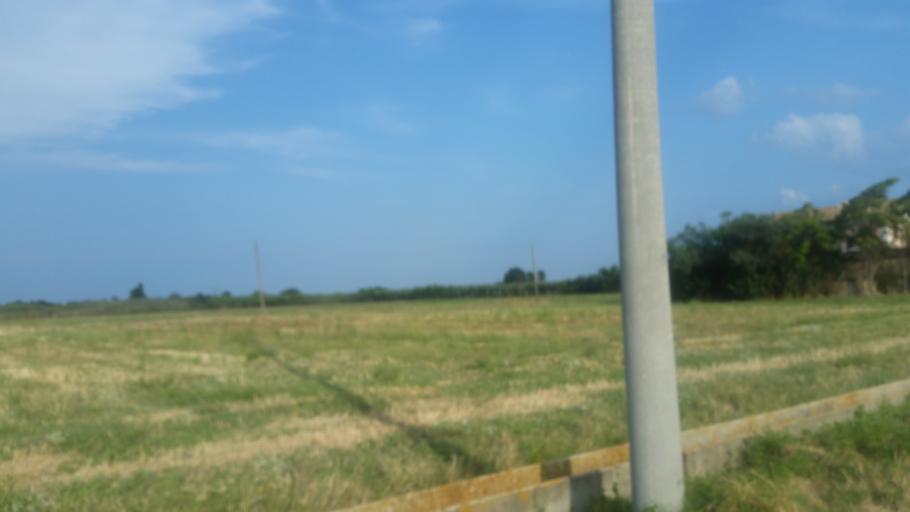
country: IT
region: The Marches
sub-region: Provincia di Ascoli Piceno
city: San Benedetto del Tronto
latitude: 42.9071
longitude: 13.9022
